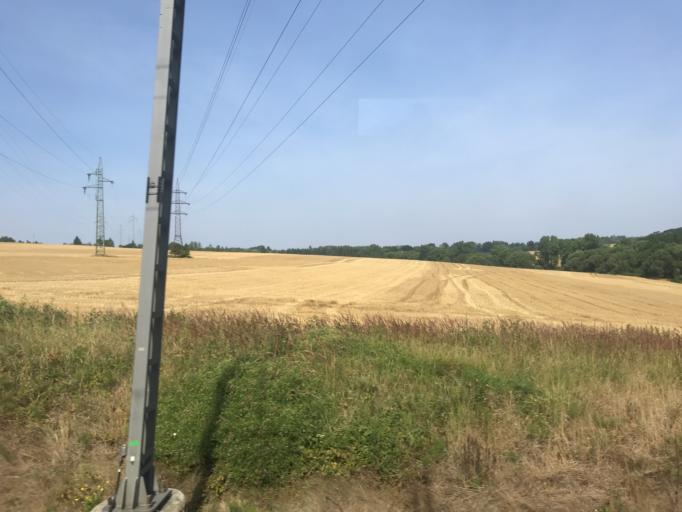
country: CZ
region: Central Bohemia
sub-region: Okres Benesov
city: Benesov
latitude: 49.7976
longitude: 14.7017
